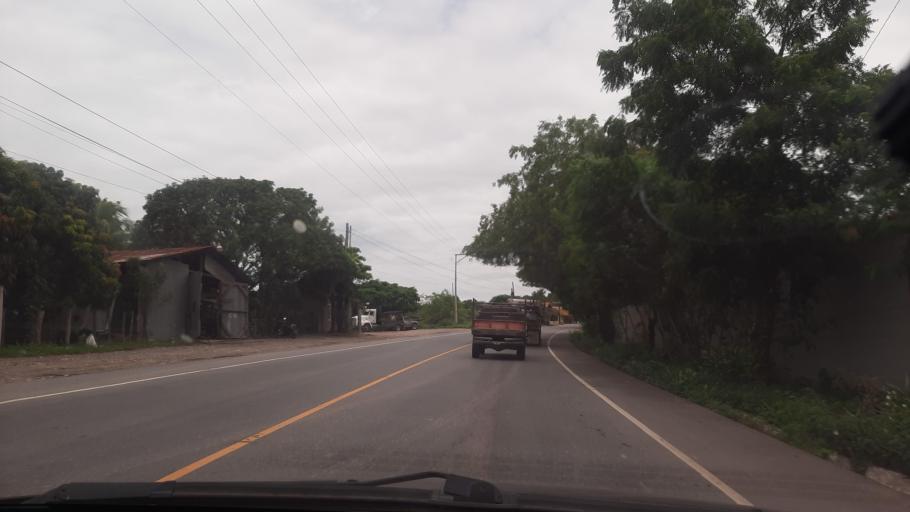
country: GT
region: Zacapa
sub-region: Municipio de Zacapa
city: Gualan
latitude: 15.1315
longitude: -89.3473
